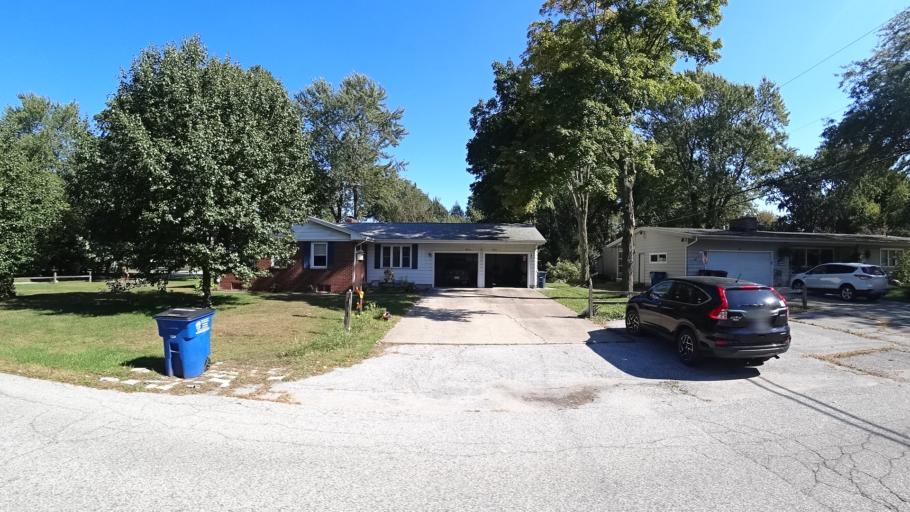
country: US
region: Indiana
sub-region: LaPorte County
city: Michigan City
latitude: 41.6906
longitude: -86.8925
